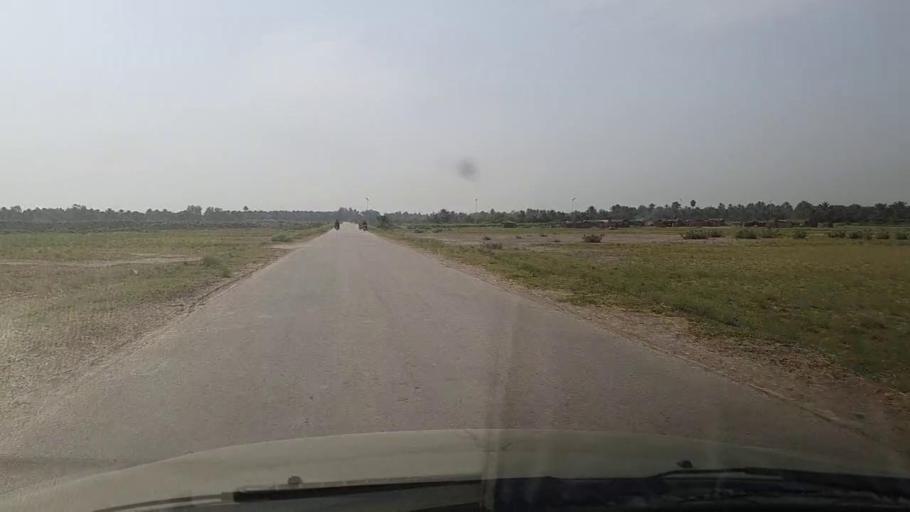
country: PK
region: Sindh
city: Gambat
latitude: 27.4608
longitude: 68.4819
